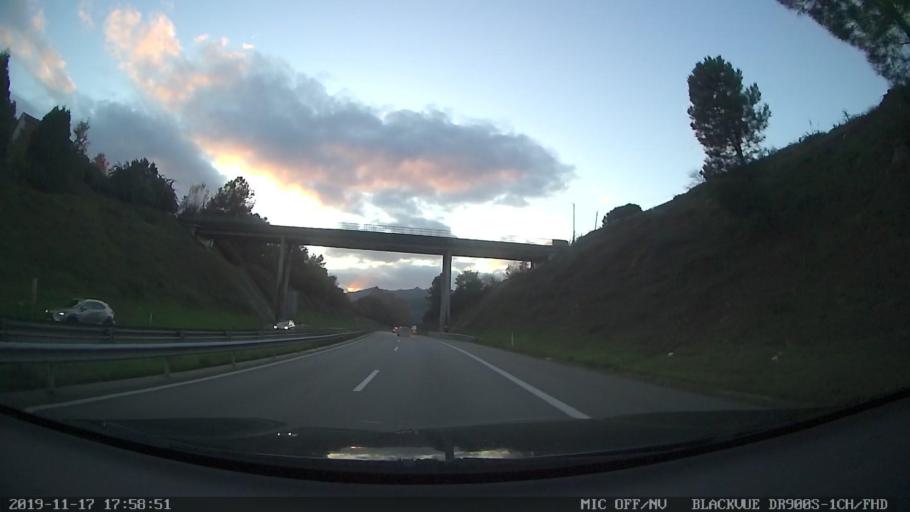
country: PT
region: Porto
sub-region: Amarante
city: Amarante
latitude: 41.2597
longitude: -8.0816
